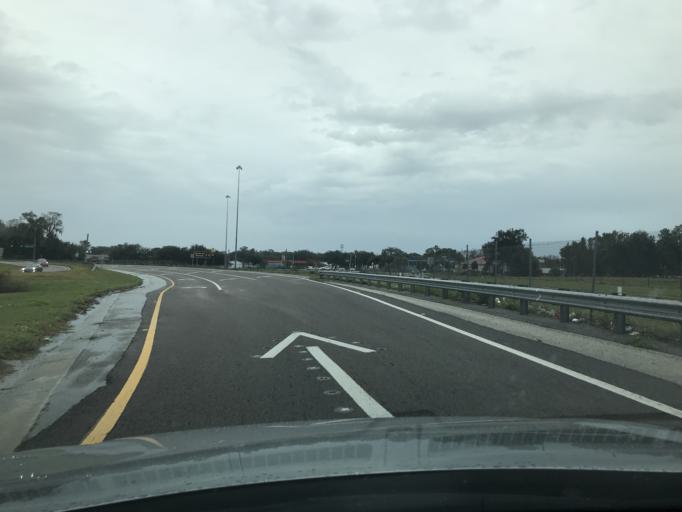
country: US
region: Florida
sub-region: Polk County
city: Winston
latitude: 28.0351
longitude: -82.0583
